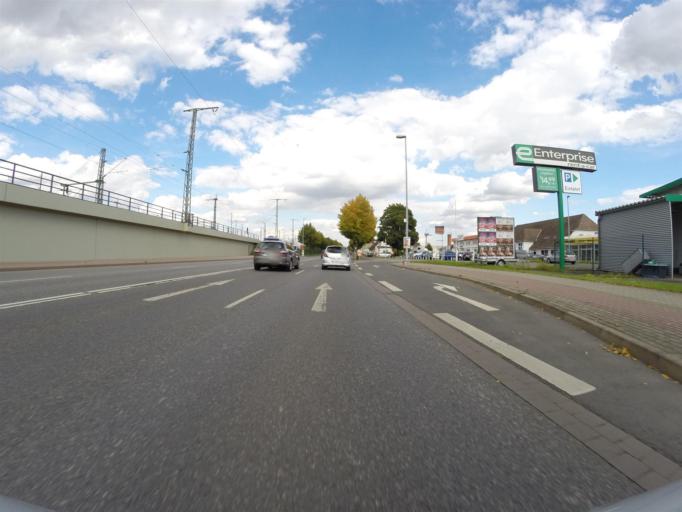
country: DE
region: Thuringia
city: Erfurt
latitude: 50.9743
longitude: 11.0585
